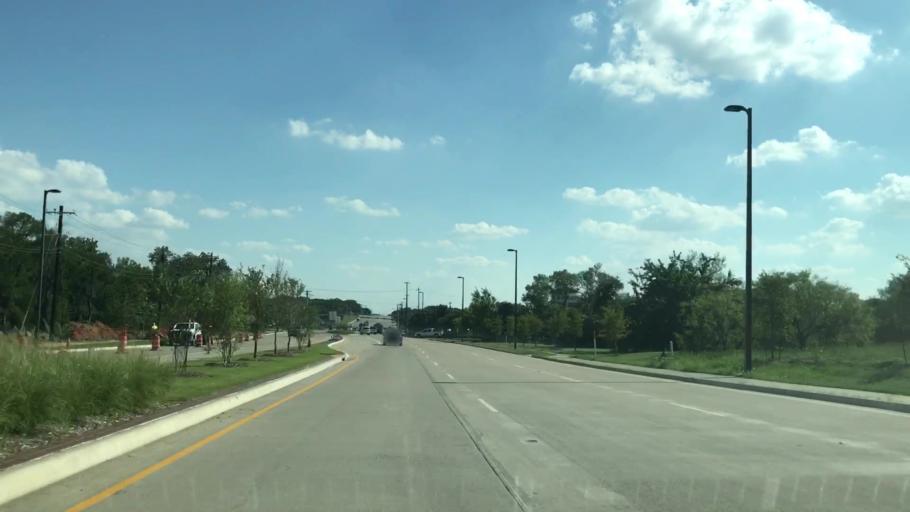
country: US
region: Texas
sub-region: Tarrant County
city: Southlake
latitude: 32.9410
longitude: -97.1860
